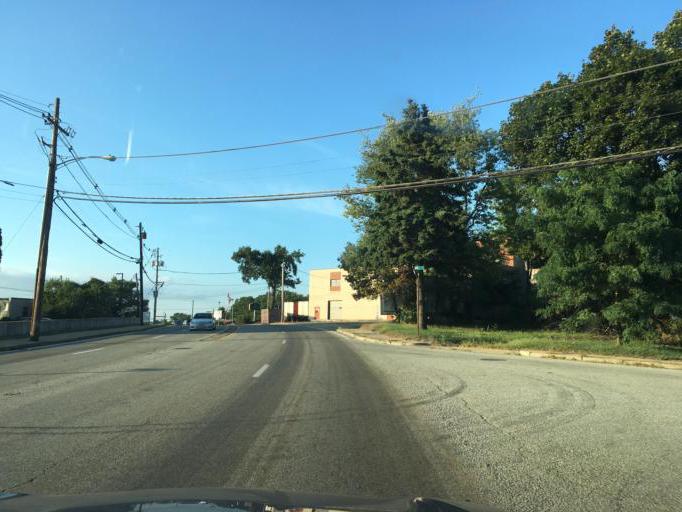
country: US
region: Rhode Island
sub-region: Providence County
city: Cranston
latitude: 41.7508
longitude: -71.4349
